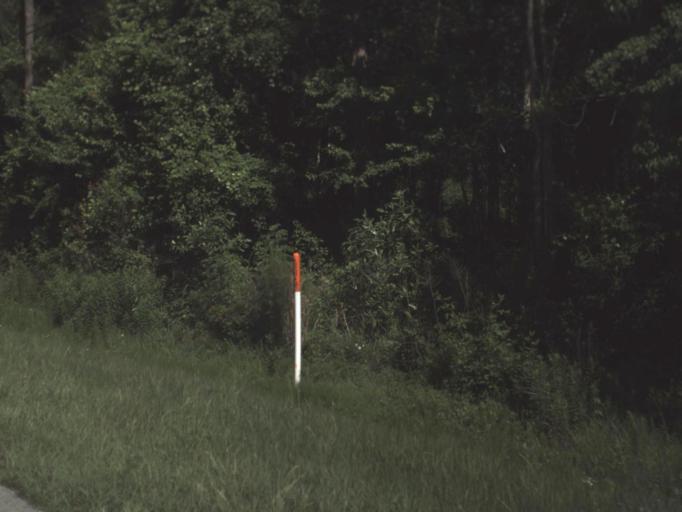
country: US
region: Florida
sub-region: Duval County
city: Baldwin
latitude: 30.3102
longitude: -81.8877
